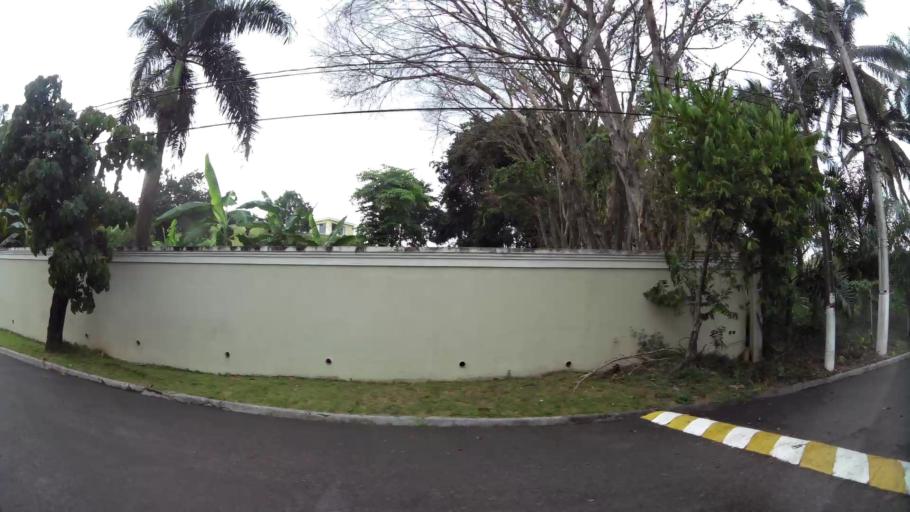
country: DO
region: Nacional
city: La Agustina
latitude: 18.5135
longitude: -69.9541
